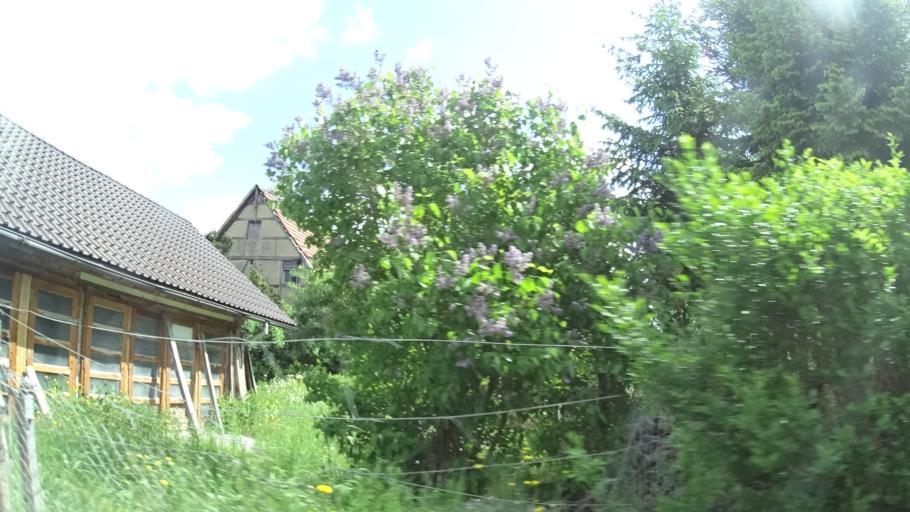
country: DE
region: Thuringia
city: Schmeheim
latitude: 50.6009
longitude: 10.5930
